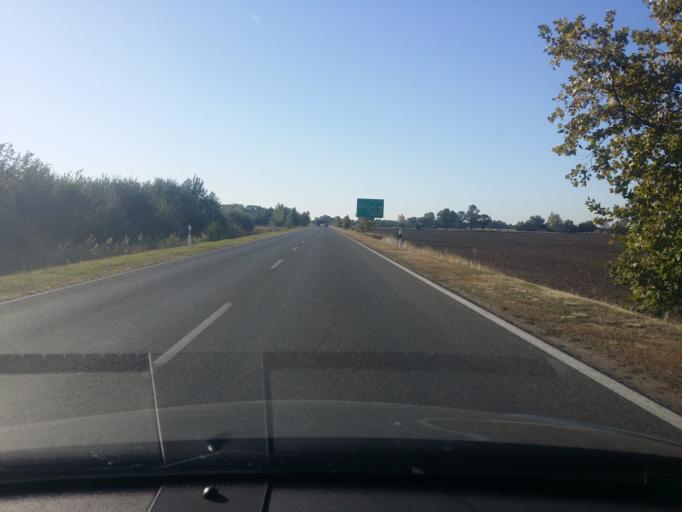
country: HU
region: Csongrad
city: Szeged
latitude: 46.2369
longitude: 20.0864
